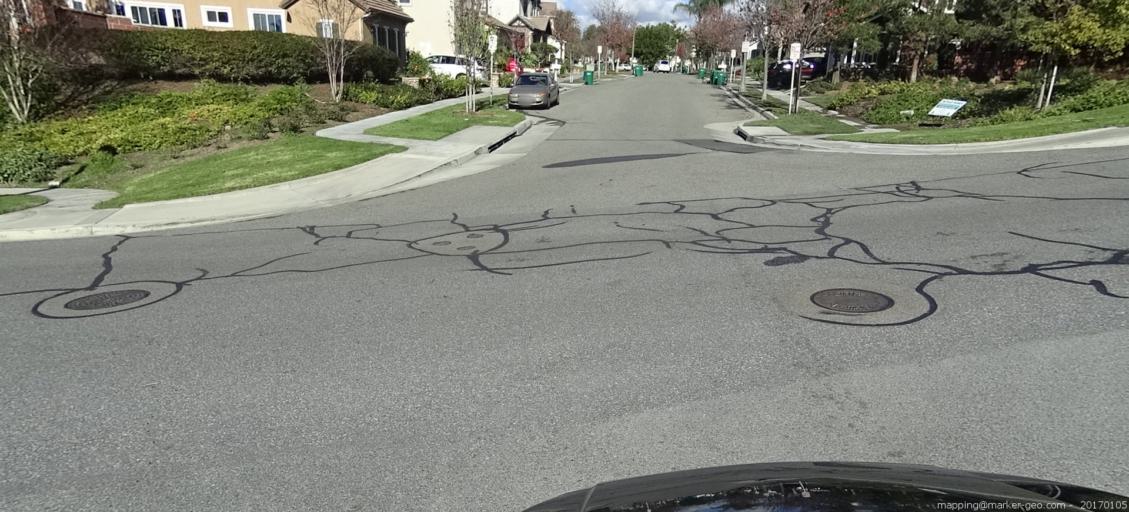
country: US
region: California
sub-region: Orange County
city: Ladera Ranch
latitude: 33.5493
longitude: -117.6318
